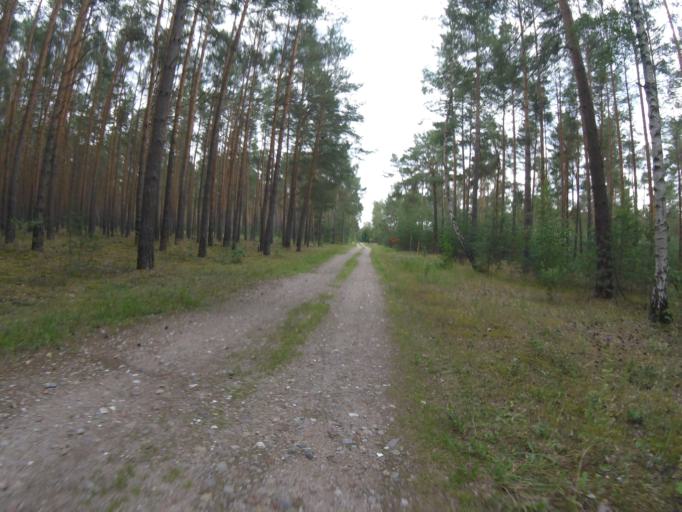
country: DE
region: Brandenburg
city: Halbe
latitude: 52.1187
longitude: 13.6990
